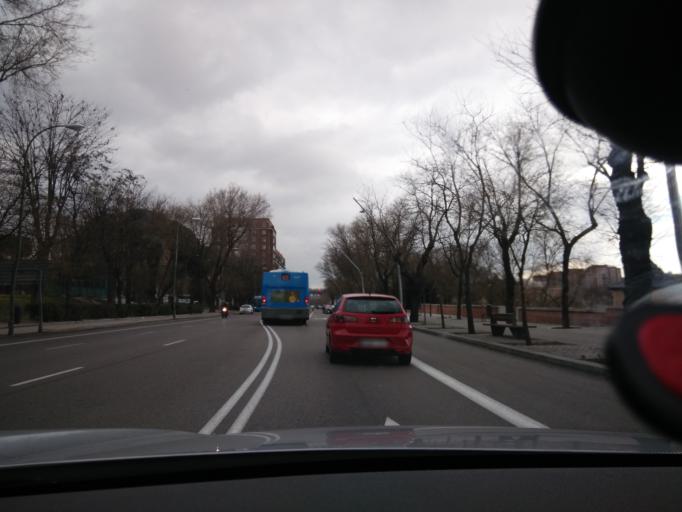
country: ES
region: Madrid
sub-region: Provincia de Madrid
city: City Center
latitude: 40.4160
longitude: -3.7207
